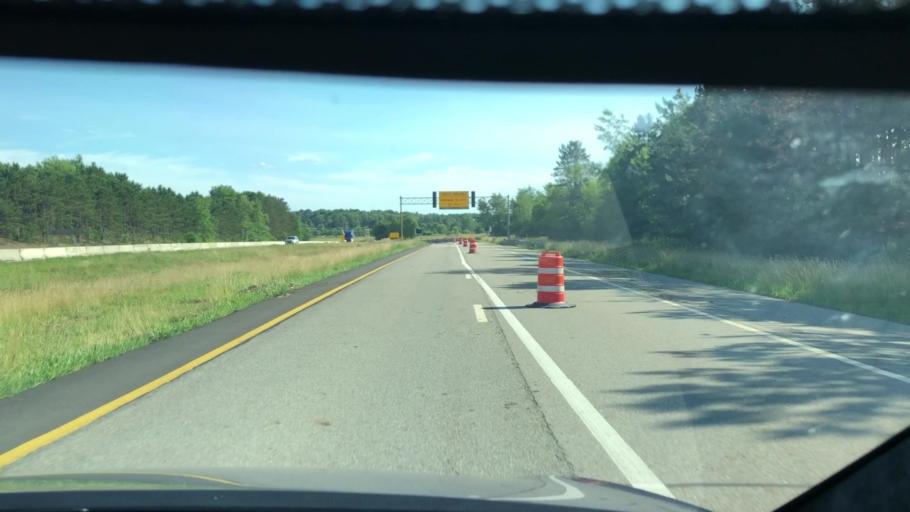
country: US
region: Ohio
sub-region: Mahoning County
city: Poland
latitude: 40.9676
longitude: -80.6388
